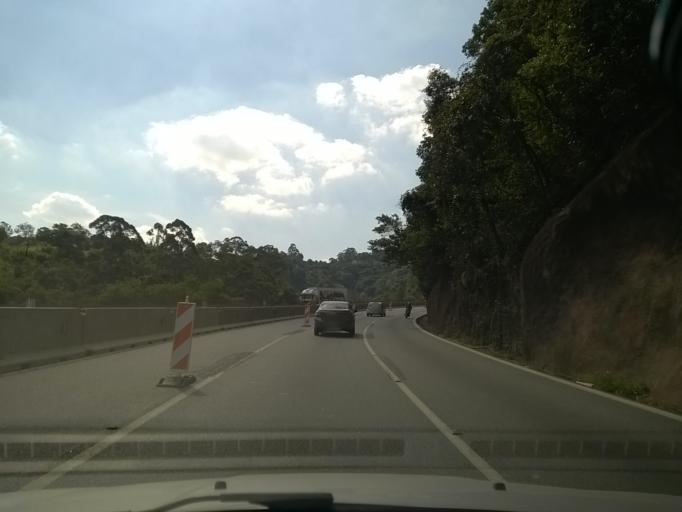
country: BR
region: Sao Paulo
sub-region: Osasco
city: Osasco
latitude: -23.4703
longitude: -46.7789
